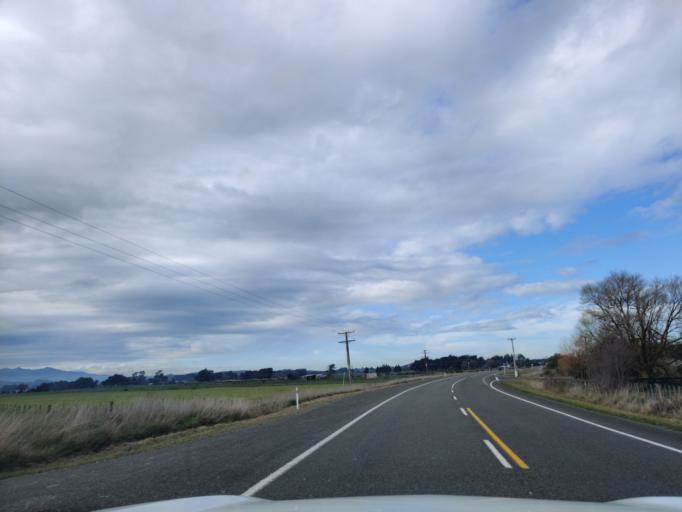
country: NZ
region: Manawatu-Wanganui
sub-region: Palmerston North City
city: Palmerston North
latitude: -40.3337
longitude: 175.8451
